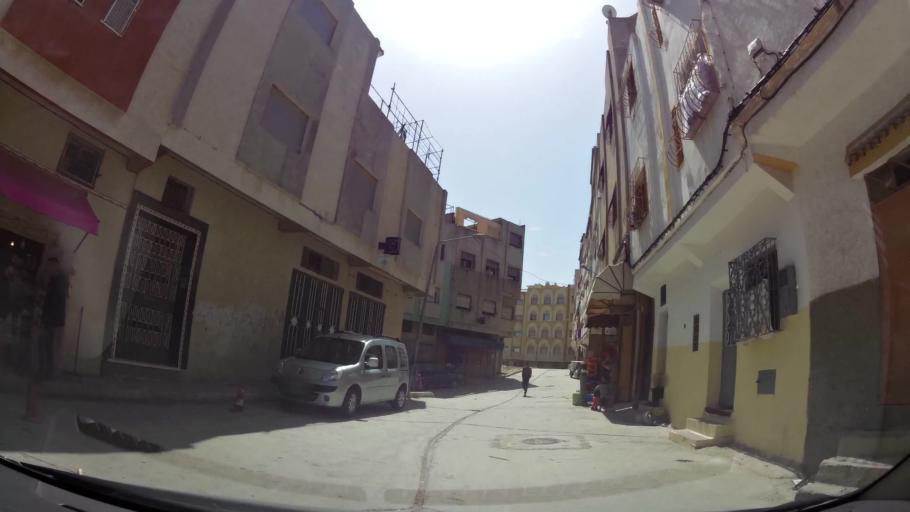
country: MA
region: Tanger-Tetouan
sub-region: Tanger-Assilah
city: Tangier
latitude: 35.7346
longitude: -5.8066
